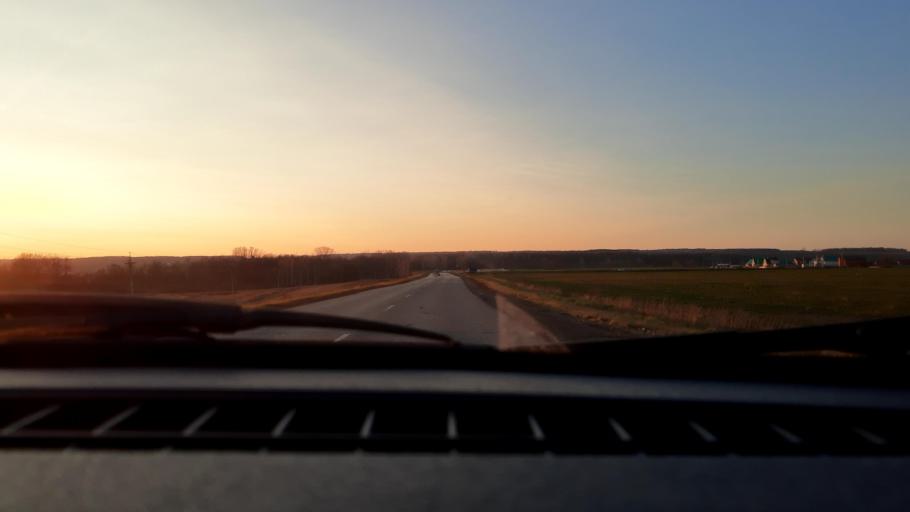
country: RU
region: Bashkortostan
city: Mikhaylovka
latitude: 54.8313
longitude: 55.9521
